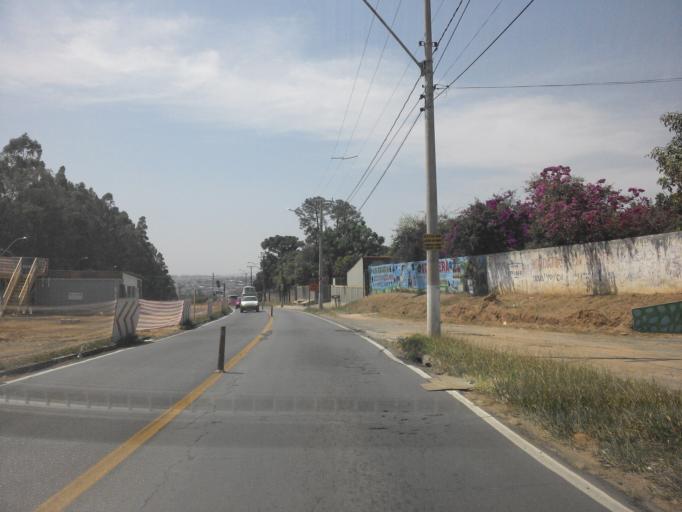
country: BR
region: Sao Paulo
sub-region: Hortolandia
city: Hortolandia
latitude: -22.9429
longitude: -47.1760
